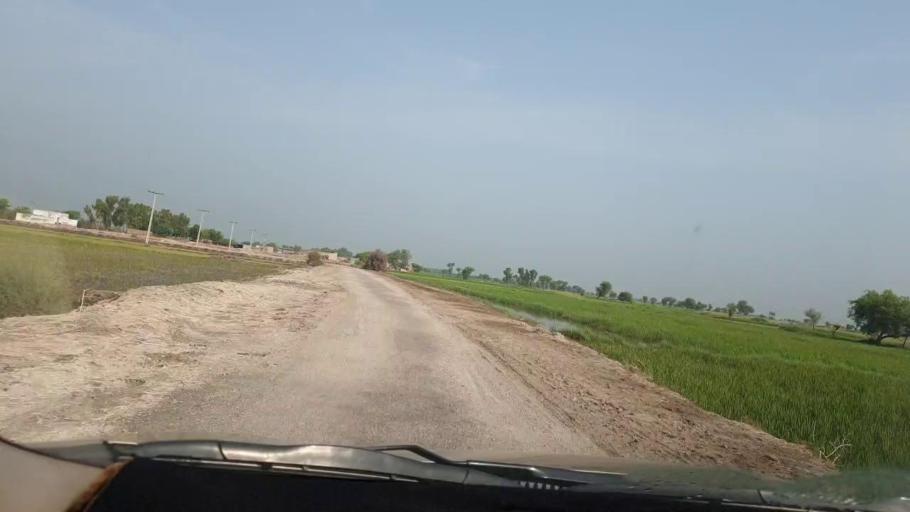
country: PK
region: Sindh
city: Goth Garelo
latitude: 27.4635
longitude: 68.0502
